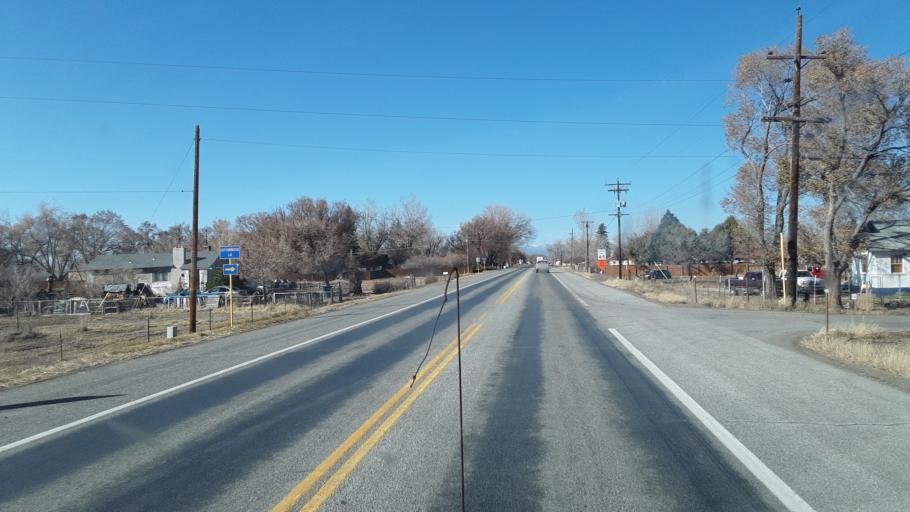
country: US
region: Colorado
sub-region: Alamosa County
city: Alamosa East
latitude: 37.4734
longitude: -105.8447
